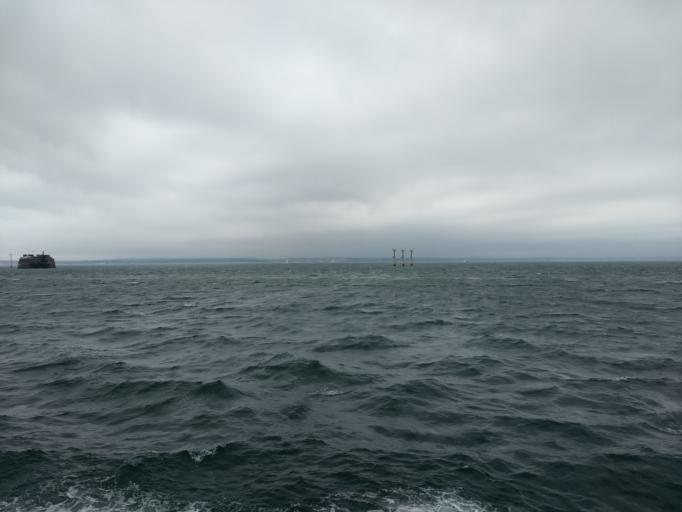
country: GB
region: England
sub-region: Portsmouth
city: Southsea
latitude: 50.7780
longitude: -1.0964
